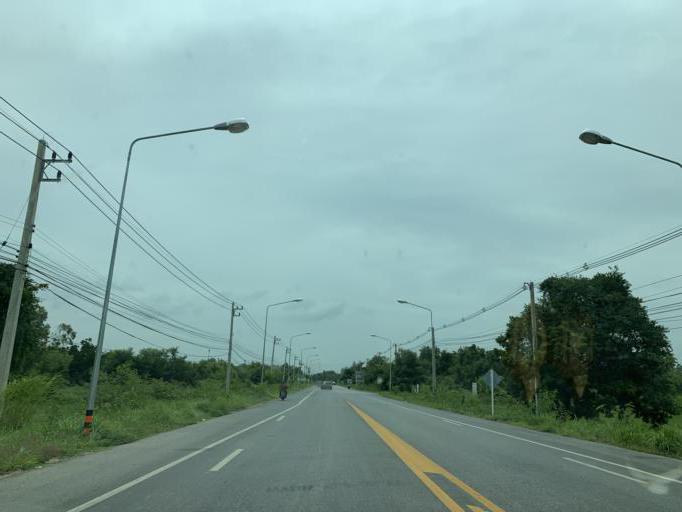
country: TH
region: Uthai Thani
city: Uthai Thani
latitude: 15.4053
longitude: 100.0229
